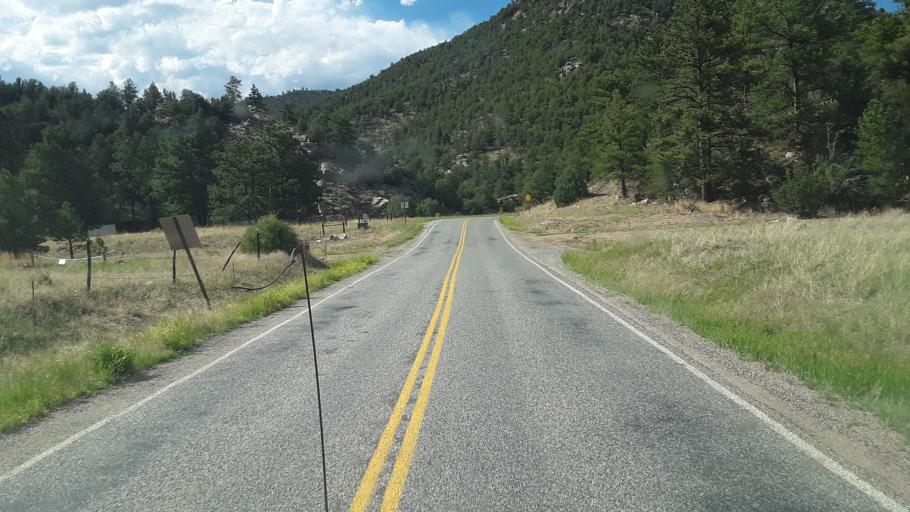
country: US
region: Colorado
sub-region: Fremont County
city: Canon City
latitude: 38.3871
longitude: -105.4552
